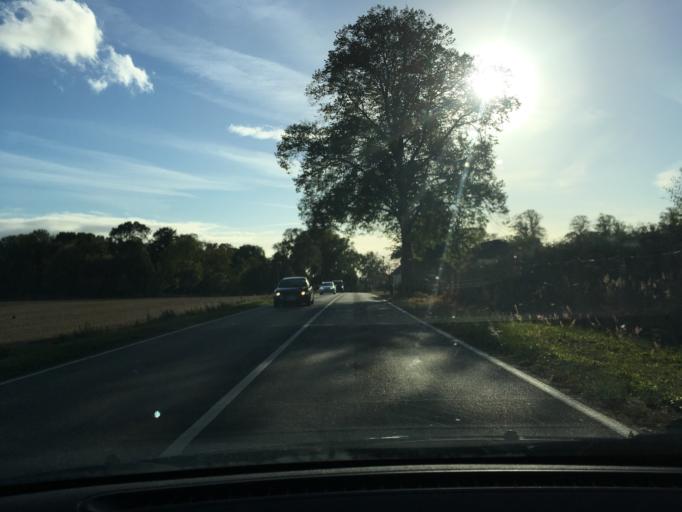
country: DE
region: Lower Saxony
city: Neu Darchau
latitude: 53.3827
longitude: 10.8938
